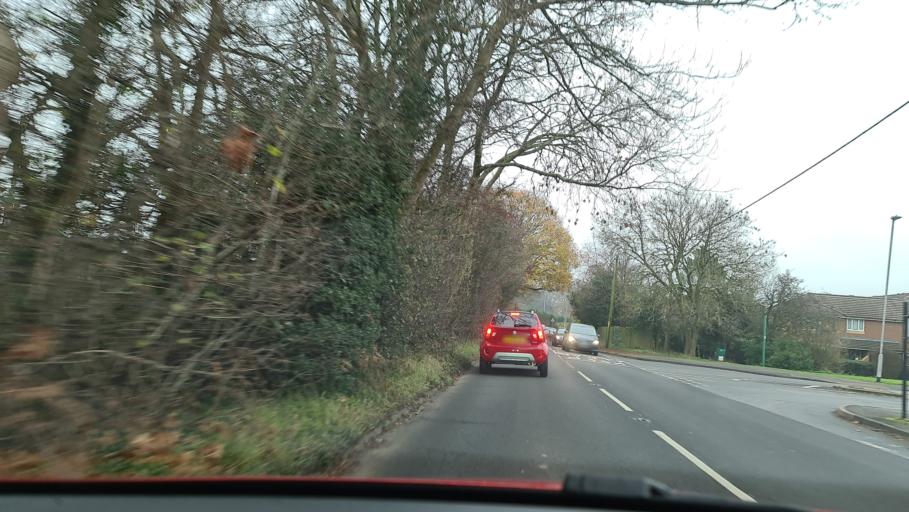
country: GB
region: England
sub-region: Buckinghamshire
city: High Wycombe
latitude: 51.6511
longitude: -0.7086
